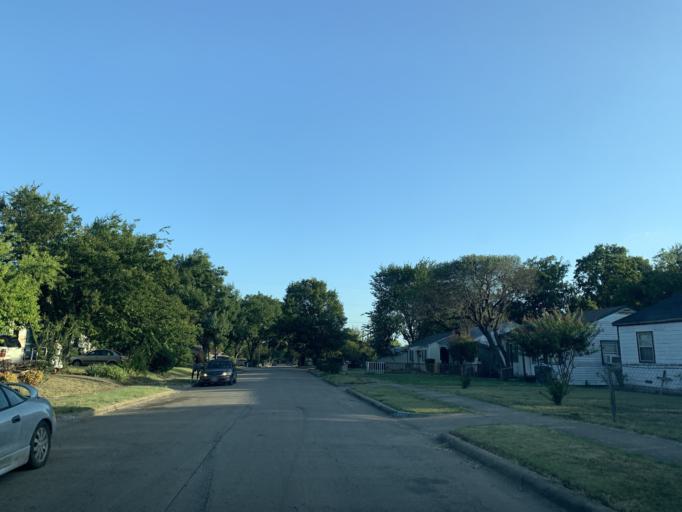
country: US
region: Texas
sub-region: Dallas County
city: Dallas
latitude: 32.7037
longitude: -96.8109
